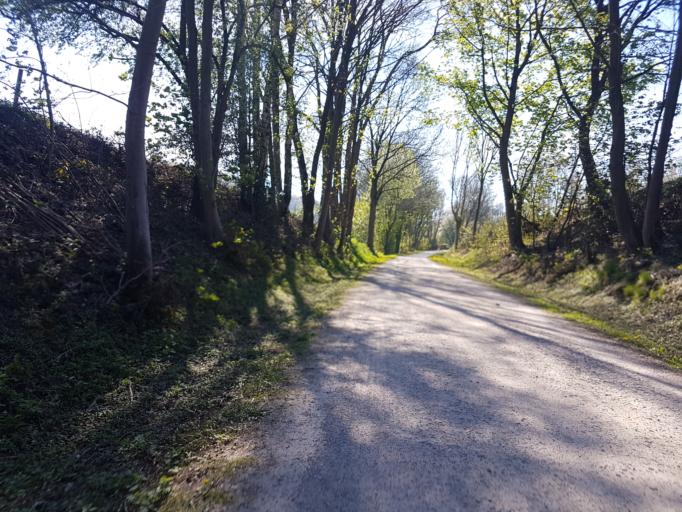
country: DE
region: North Rhine-Westphalia
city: Hattingen
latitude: 51.3845
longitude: 7.1921
